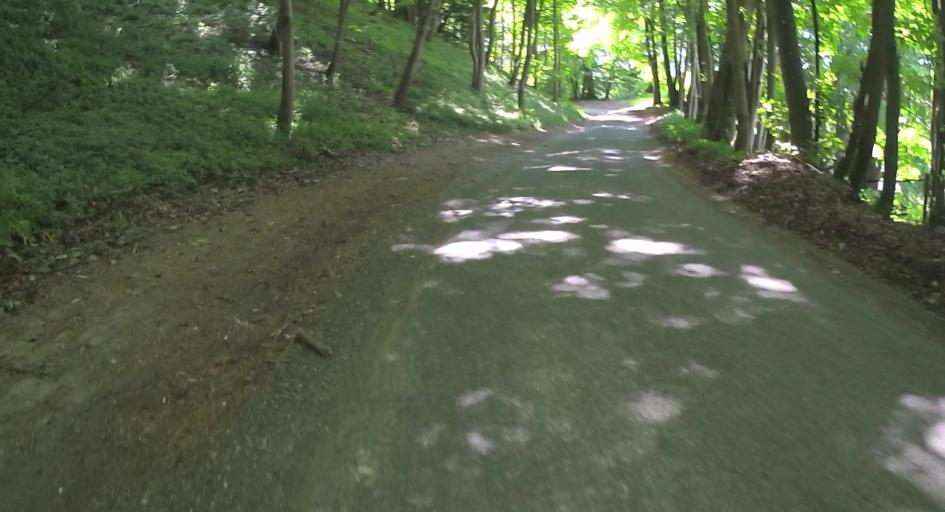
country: GB
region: England
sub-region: Hampshire
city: Kingsclere
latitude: 51.3092
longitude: -1.2948
